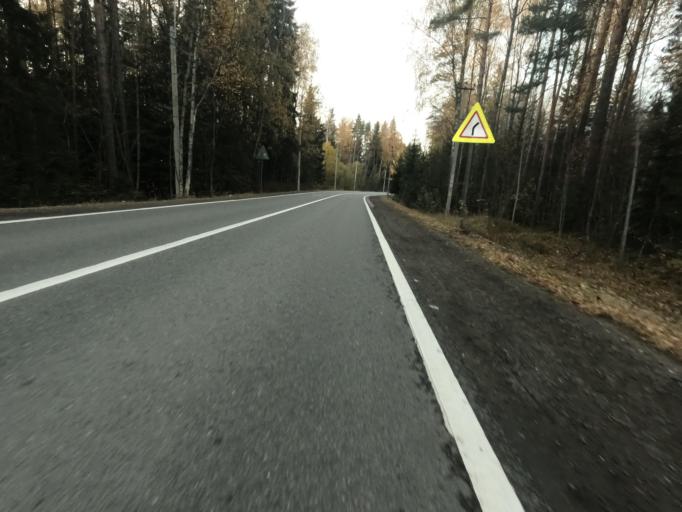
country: RU
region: St.-Petersburg
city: Repino
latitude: 60.1919
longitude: 29.8573
